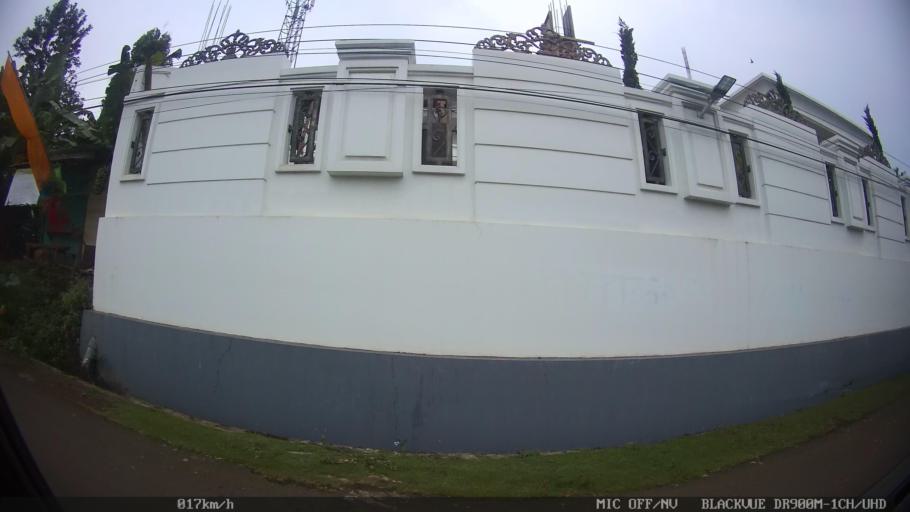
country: ID
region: Lampung
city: Kedaton
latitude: -5.4017
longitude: 105.2418
